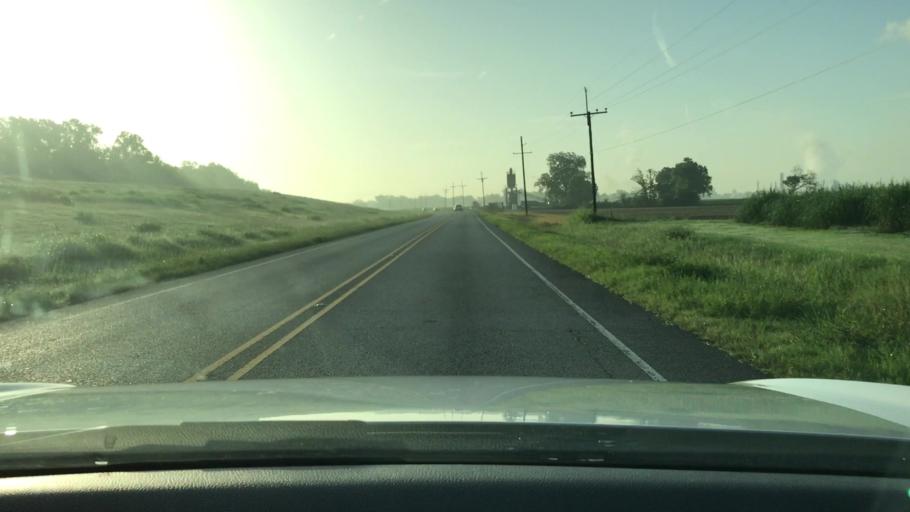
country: US
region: Louisiana
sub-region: Iberville Parish
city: Plaquemine
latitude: 30.2731
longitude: -91.2023
